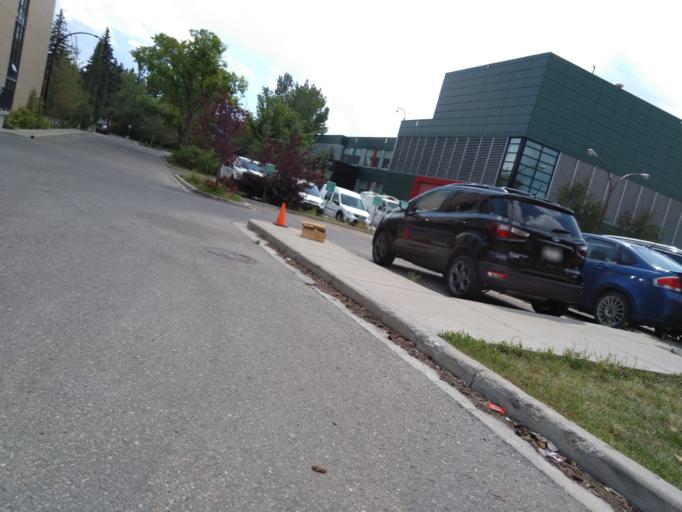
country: CA
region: Alberta
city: Calgary
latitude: 51.0756
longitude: -114.1380
